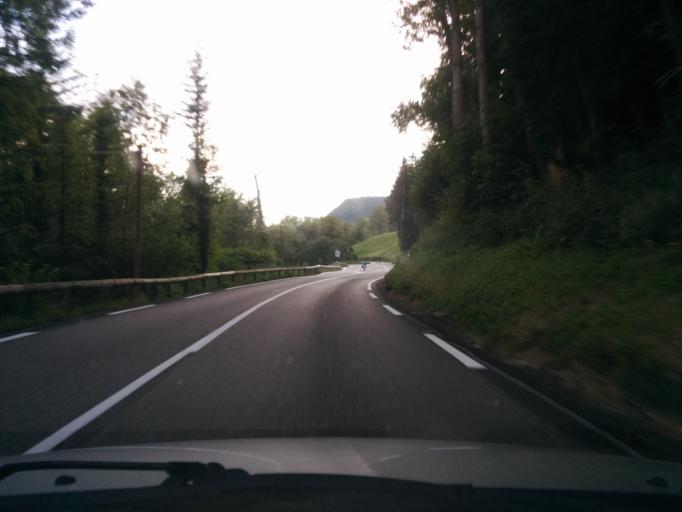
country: FR
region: Rhone-Alpes
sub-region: Departement de l'Isere
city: La Buisse
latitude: 45.3404
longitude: 5.6637
